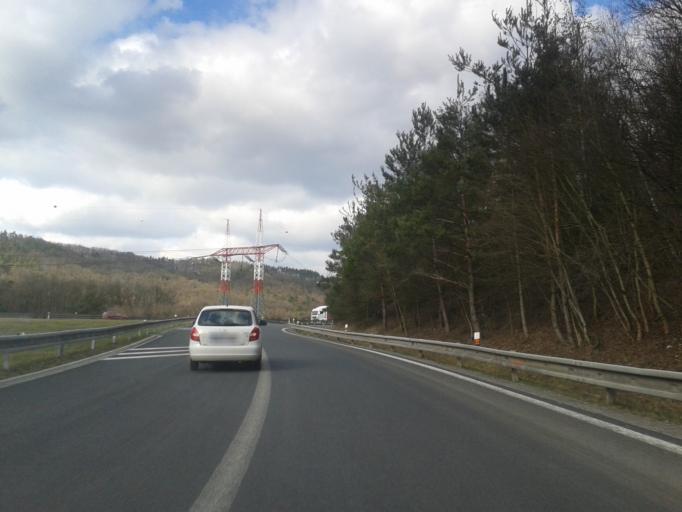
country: CZ
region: Central Bohemia
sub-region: Okres Beroun
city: Beroun
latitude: 49.9748
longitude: 14.1106
